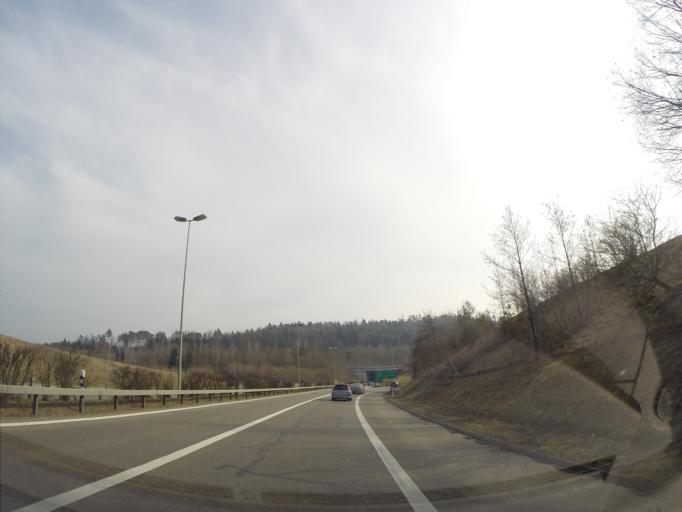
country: CH
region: Zurich
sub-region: Bezirk Winterthur
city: Wuelflingen (Kreis 6) / Lindenplatz
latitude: 47.5259
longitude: 8.7006
